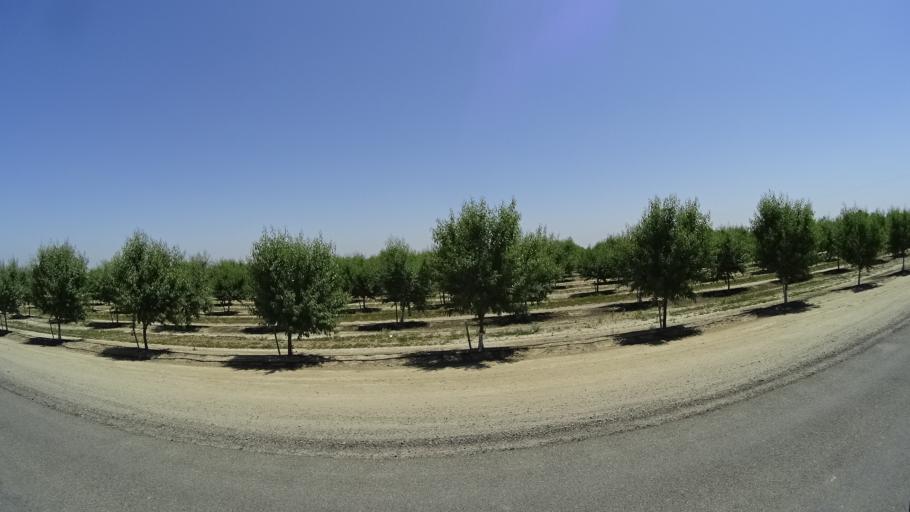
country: US
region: California
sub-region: Kings County
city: Lemoore
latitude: 36.2808
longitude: -119.7629
